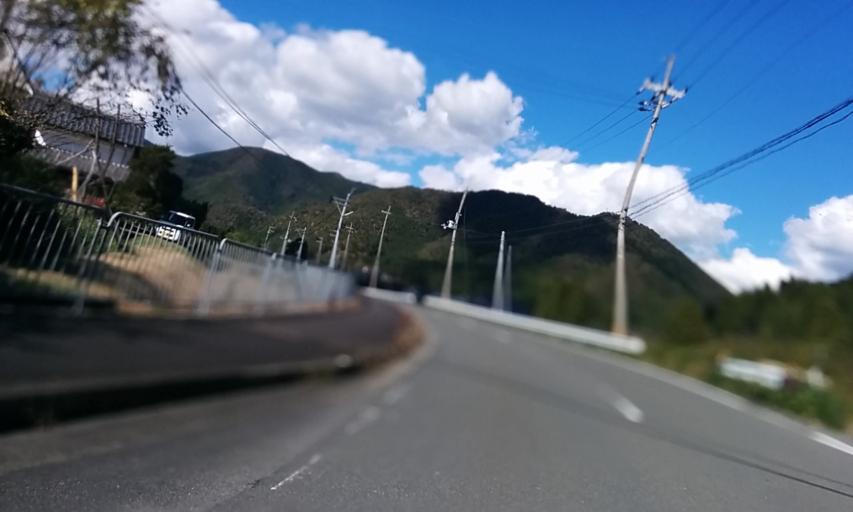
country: JP
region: Kyoto
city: Kameoka
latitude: 35.2660
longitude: 135.5505
